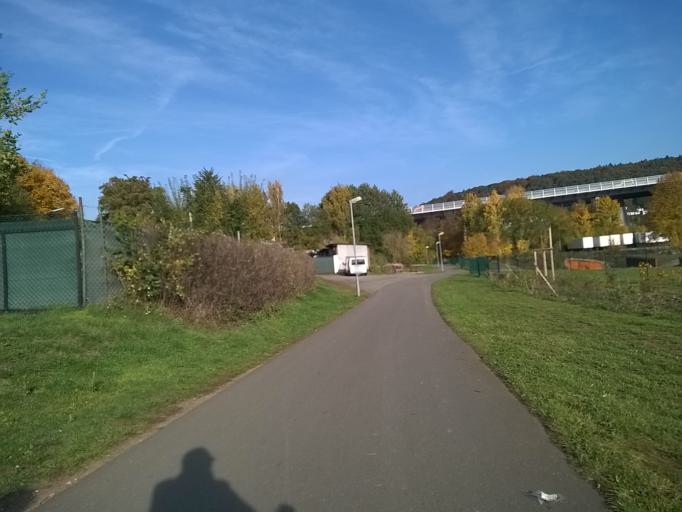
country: DE
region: Rheinland-Pfalz
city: Kaiserslautern
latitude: 49.4534
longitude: 7.7469
